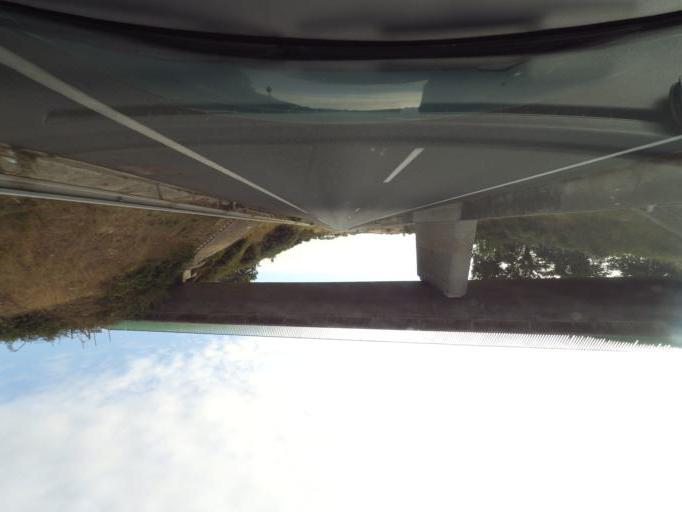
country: FR
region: Poitou-Charentes
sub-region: Departement des Deux-Sevres
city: Saint-Pierre-des-Echaubrognes
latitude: 46.9381
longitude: -0.7489
